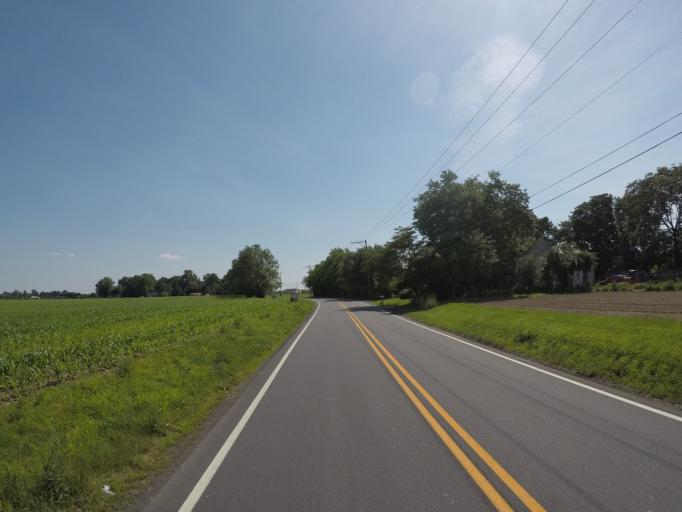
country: US
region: Delaware
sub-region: New Castle County
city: Glasgow
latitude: 39.5253
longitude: -75.7457
